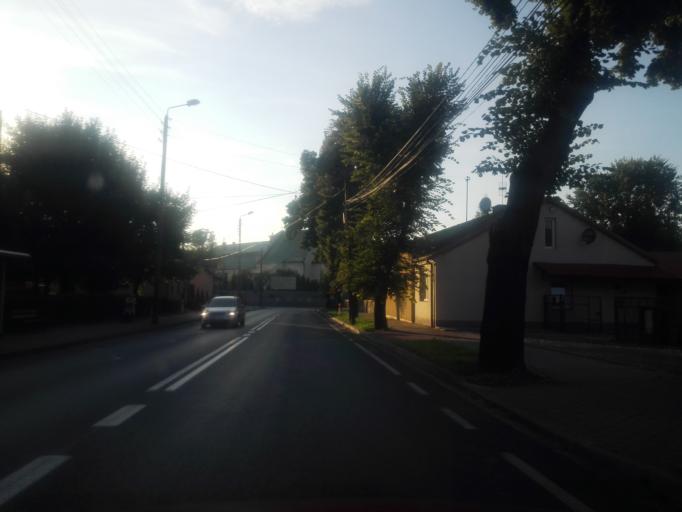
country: PL
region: Lodz Voivodeship
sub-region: Powiat wielunski
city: Wielun
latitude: 51.2164
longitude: 18.5745
